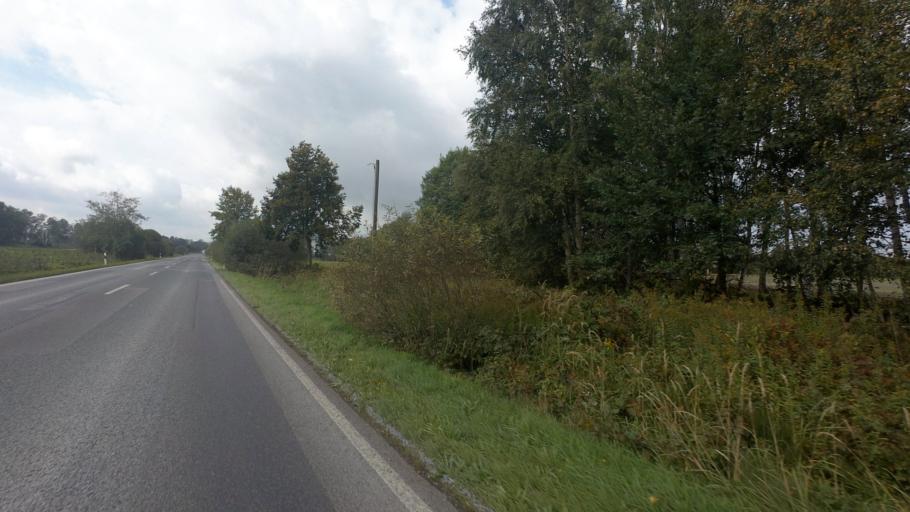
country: DE
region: Brandenburg
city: Plessa
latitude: 51.4686
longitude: 13.6488
